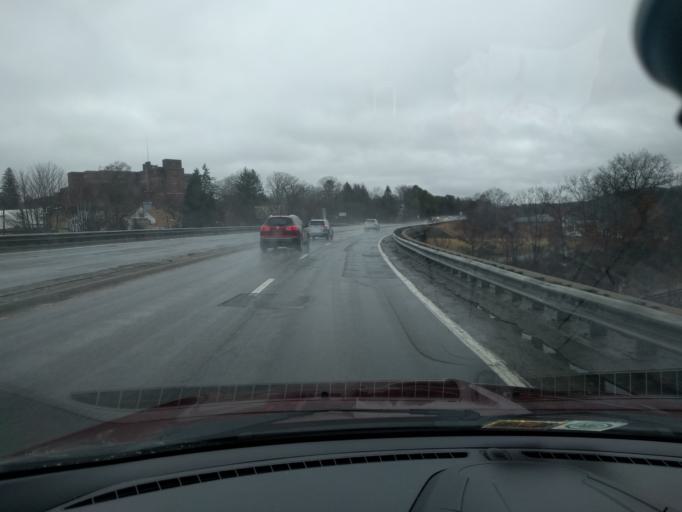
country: US
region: West Virginia
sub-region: Raleigh County
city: Mabscott
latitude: 37.7657
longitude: -81.2036
